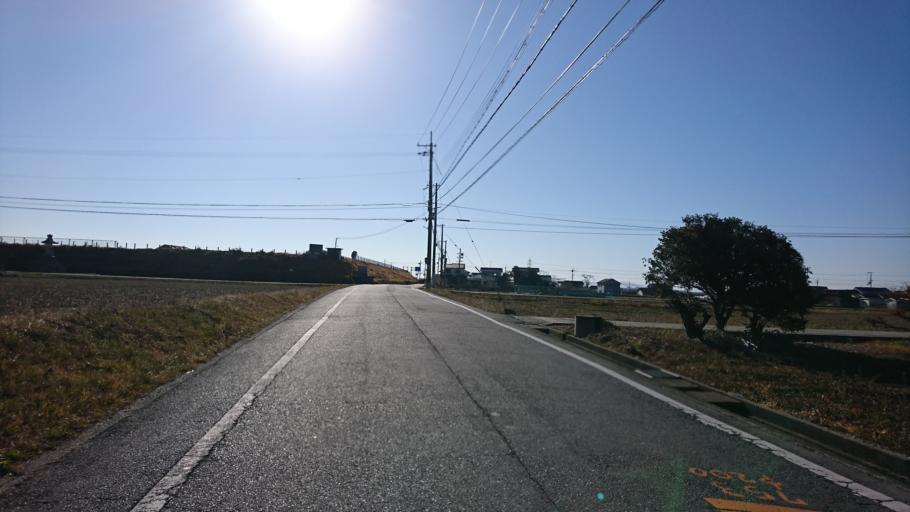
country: JP
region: Hyogo
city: Miki
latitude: 34.7396
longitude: 134.9435
